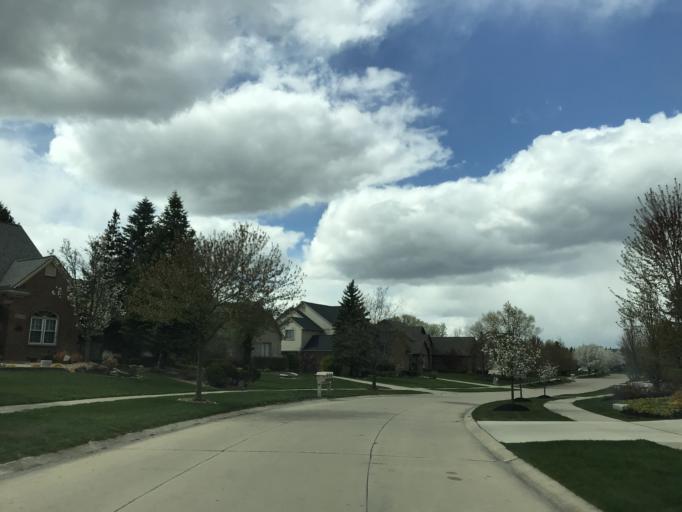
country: US
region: Michigan
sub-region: Wayne County
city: Plymouth
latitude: 42.3779
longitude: -83.5188
